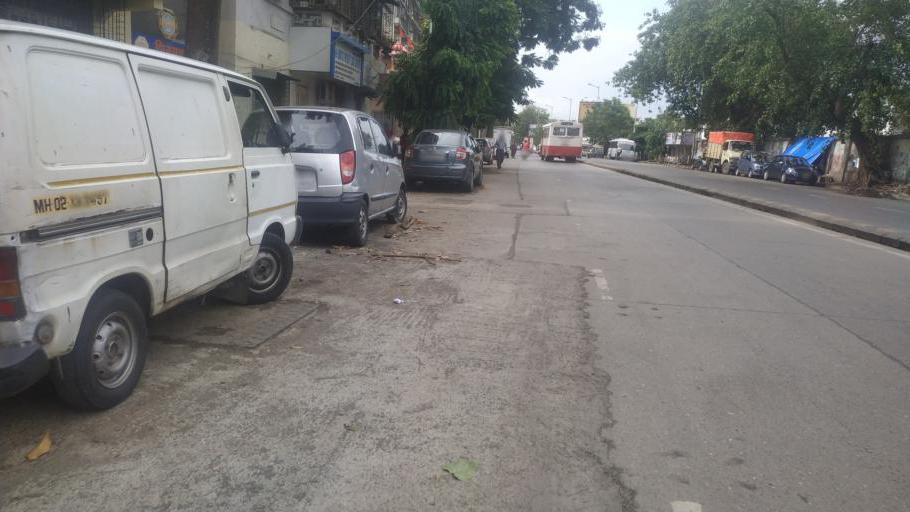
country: IN
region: Maharashtra
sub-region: Mumbai Suburban
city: Mumbai
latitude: 19.0307
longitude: 72.8472
